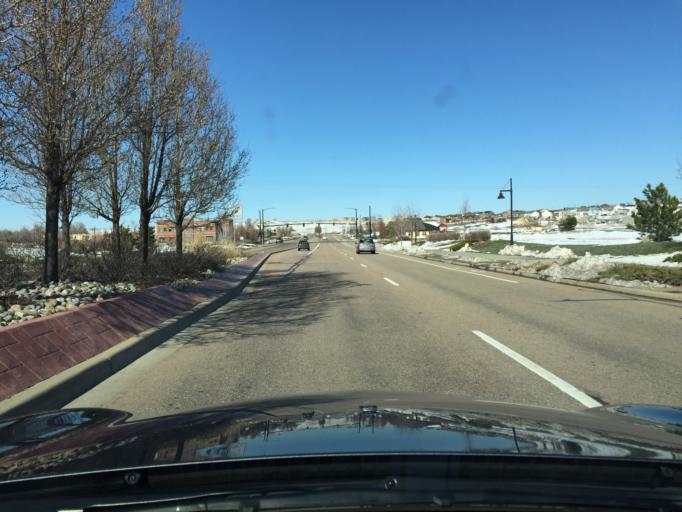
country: US
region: Colorado
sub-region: Boulder County
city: Erie
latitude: 40.0394
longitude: -105.0483
